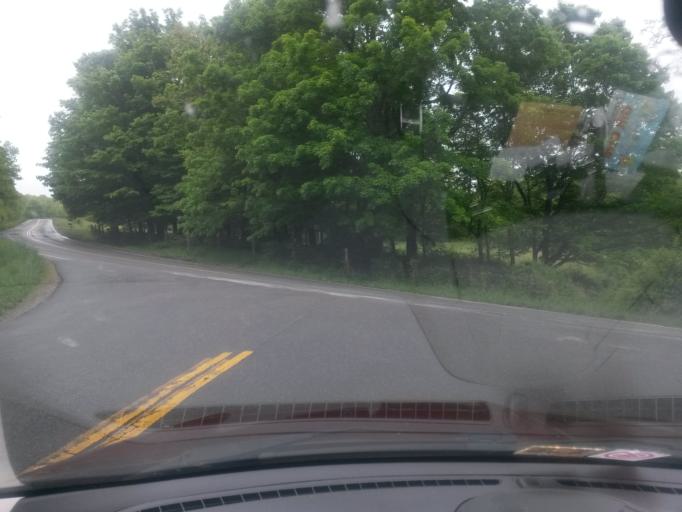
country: US
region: Virginia
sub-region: Floyd County
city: Floyd
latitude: 36.7750
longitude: -80.3908
